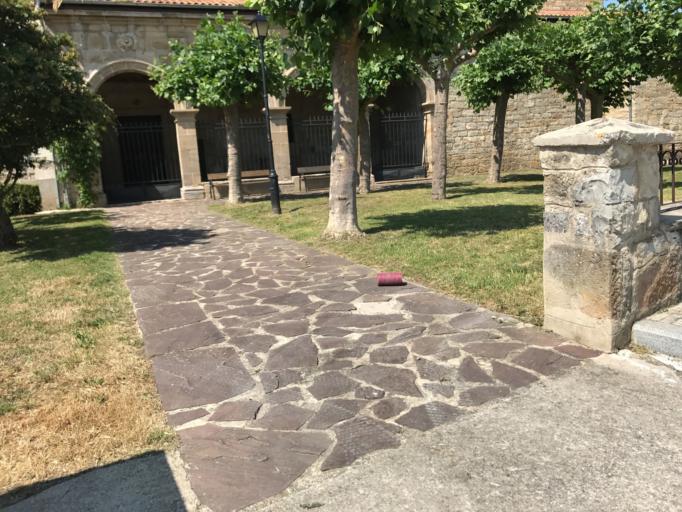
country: ES
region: Basque Country
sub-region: Provincia de Alava
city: Gasteiz / Vitoria
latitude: 42.8781
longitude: -2.6574
